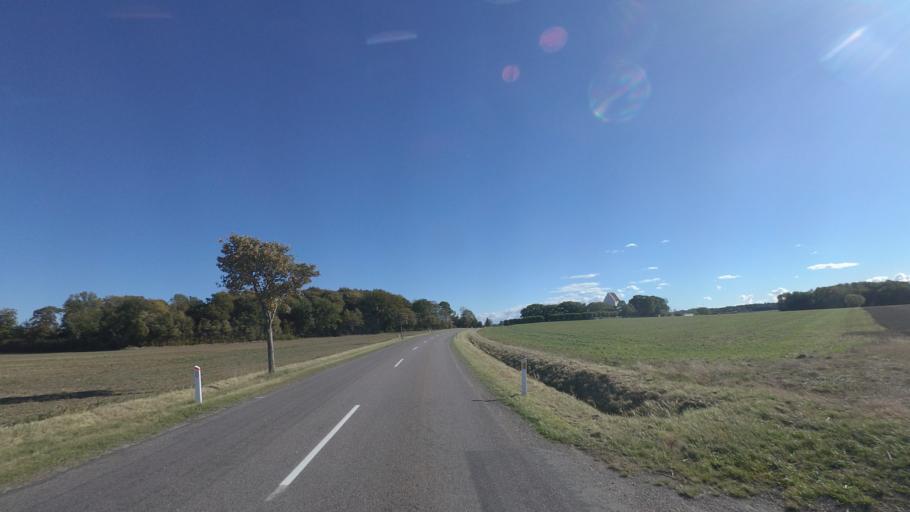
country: DK
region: Capital Region
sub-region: Bornholm Kommune
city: Nexo
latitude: 55.1199
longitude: 15.1031
